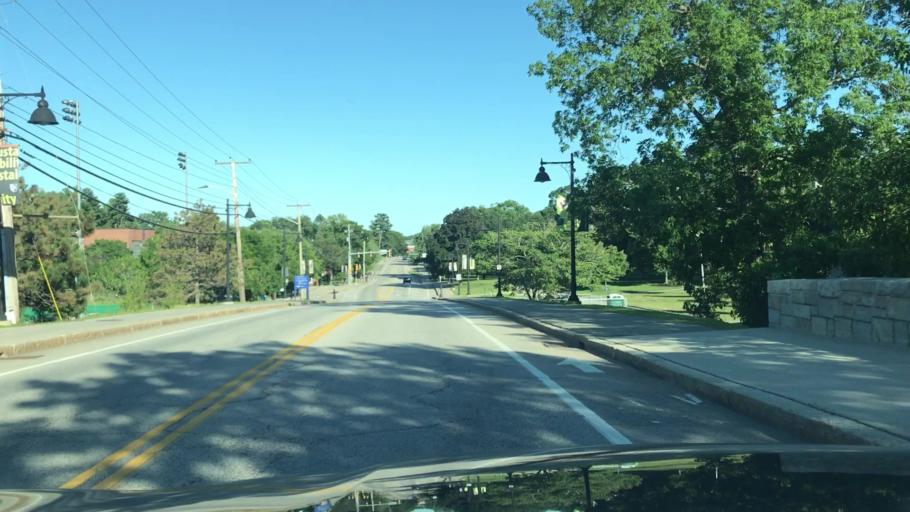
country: US
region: New Hampshire
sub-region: Strafford County
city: Durham
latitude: 43.1389
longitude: -70.9363
